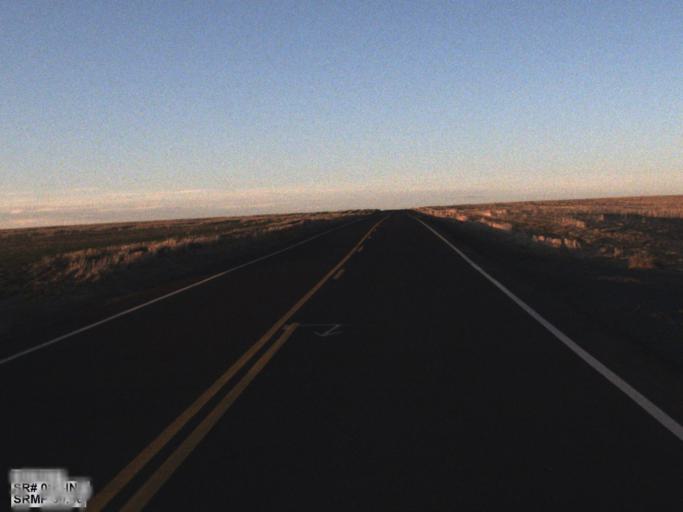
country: US
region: Washington
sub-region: Adams County
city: Ritzville
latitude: 46.9928
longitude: -118.6637
